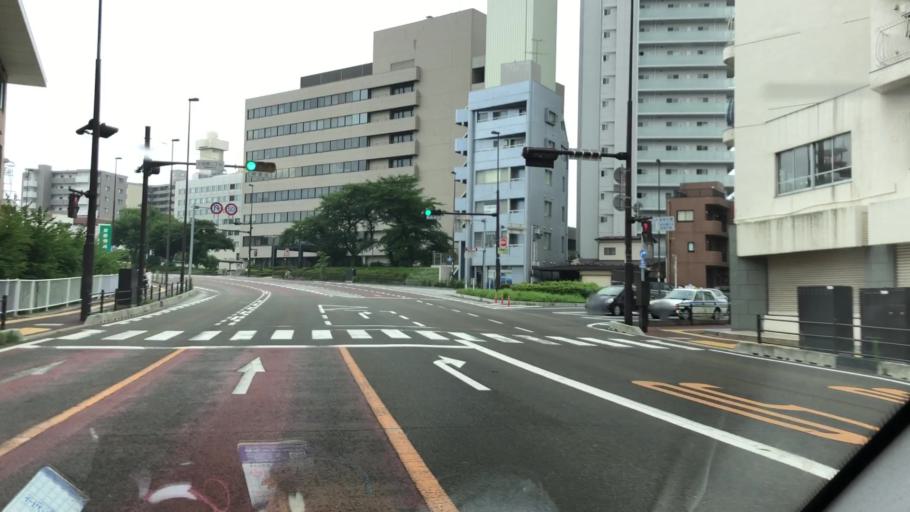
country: JP
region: Miyagi
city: Sendai-shi
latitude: 38.2638
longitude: 140.8951
